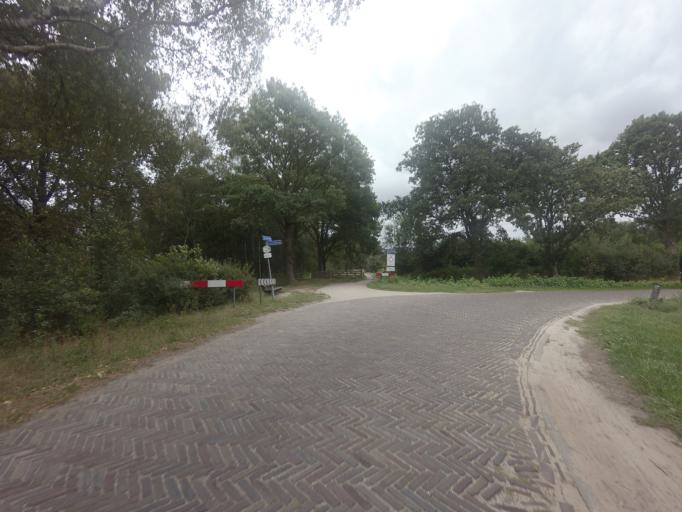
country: NL
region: Drenthe
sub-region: Gemeente Westerveld
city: Dwingeloo
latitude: 52.8825
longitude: 6.2645
